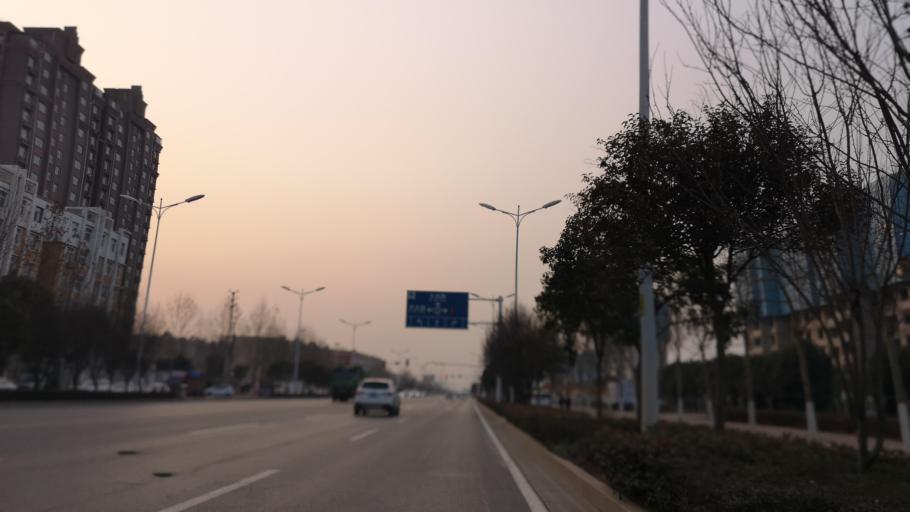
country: CN
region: Henan Sheng
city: Zhongyuanlu
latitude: 35.7894
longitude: 115.0843
